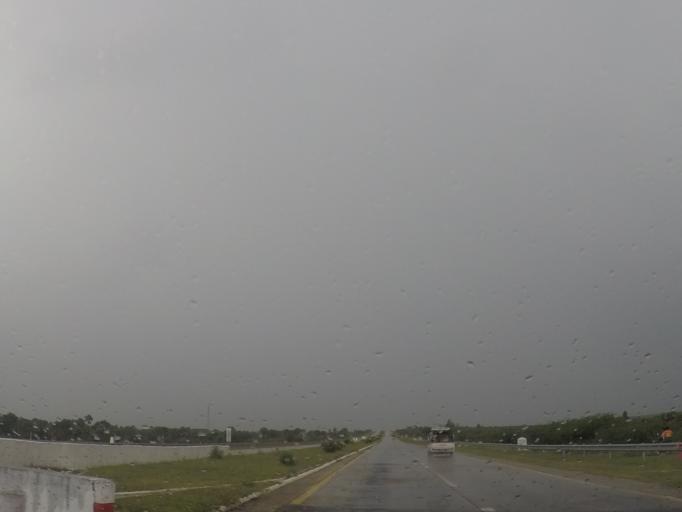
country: MM
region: Mandalay
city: Meiktila
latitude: 21.0167
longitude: 95.7862
